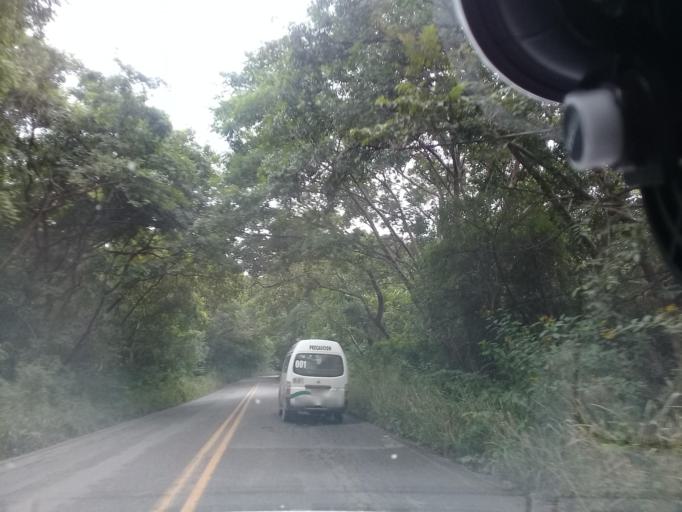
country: MX
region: Hidalgo
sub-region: Huejutla de Reyes
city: Parque de Poblamiento Solidaridad
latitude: 21.1984
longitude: -98.3890
